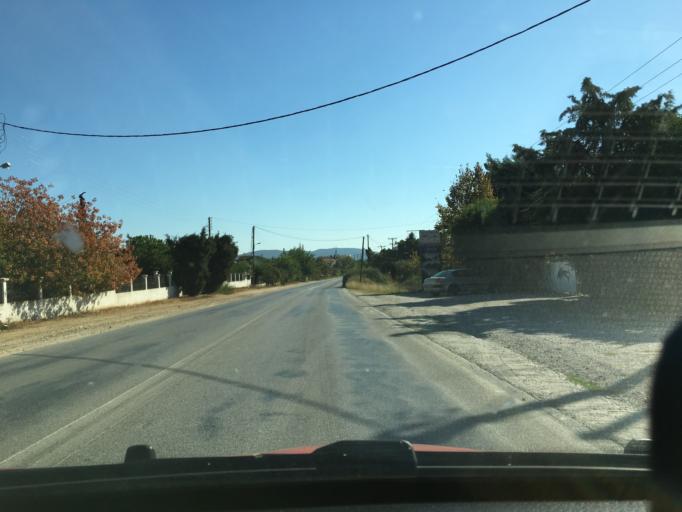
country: GR
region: Central Macedonia
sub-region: Nomos Chalkidikis
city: Ormylia
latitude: 40.2613
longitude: 23.4952
